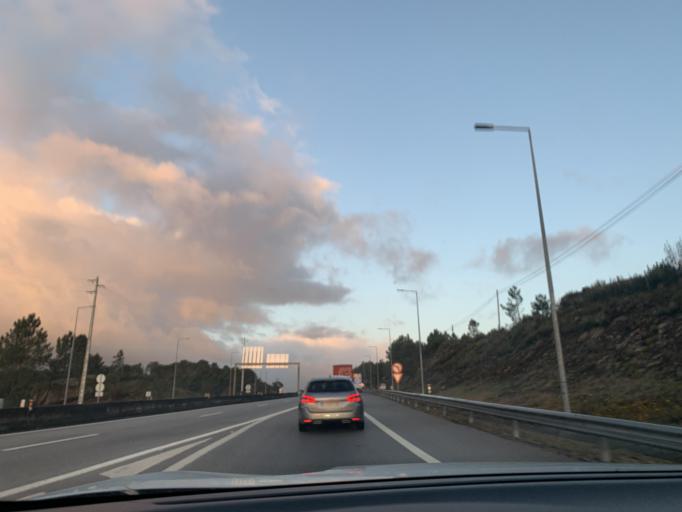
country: PT
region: Viseu
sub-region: Viseu
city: Viseu
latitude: 40.6233
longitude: -7.9223
